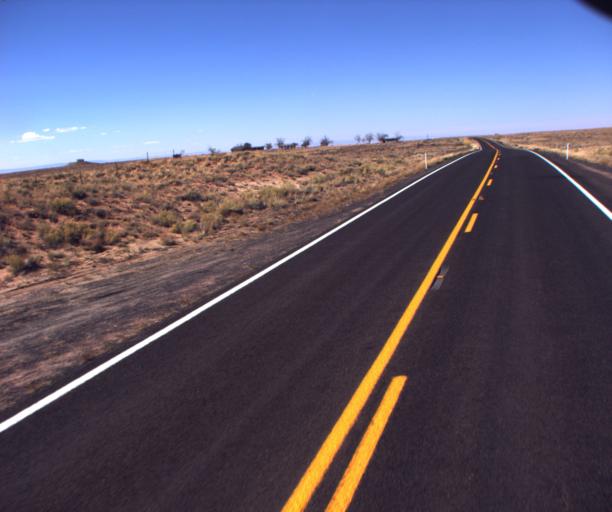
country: US
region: Arizona
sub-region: Coconino County
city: Tuba City
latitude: 35.9585
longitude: -110.9343
